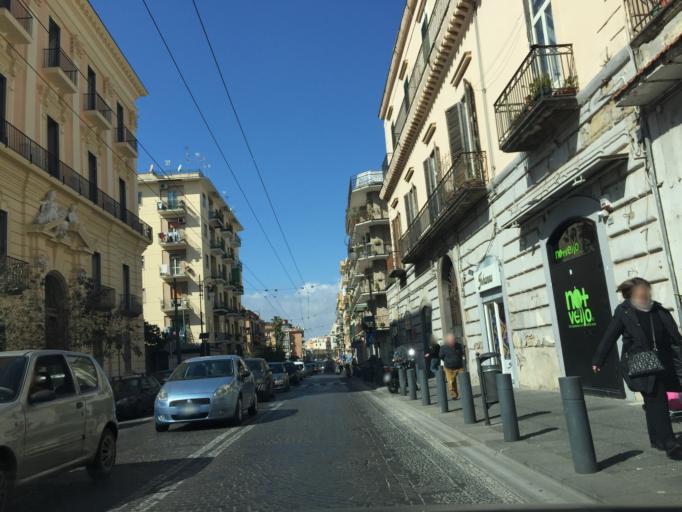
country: IT
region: Campania
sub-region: Provincia di Napoli
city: Portici
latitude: 40.8166
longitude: 14.3333
